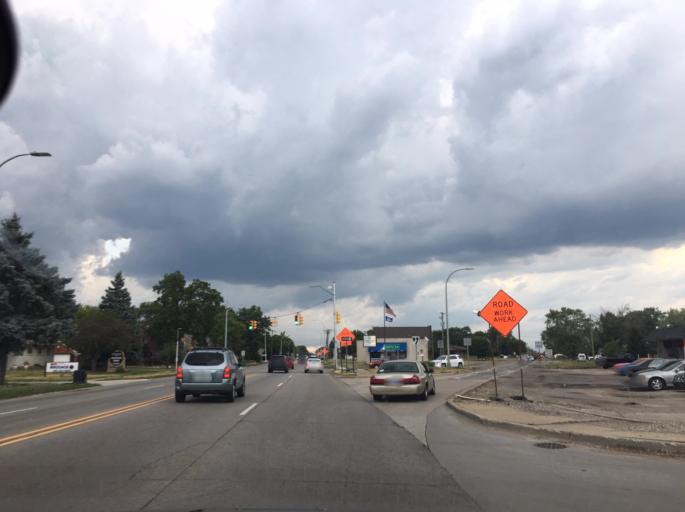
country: US
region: Michigan
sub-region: Macomb County
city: Fraser
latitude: 42.5331
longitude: -82.9494
